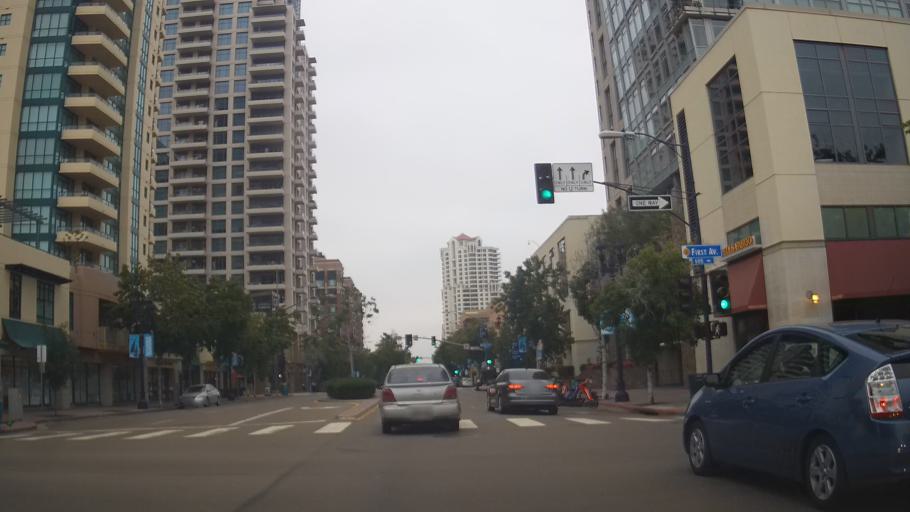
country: US
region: California
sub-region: San Diego County
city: San Diego
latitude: 32.7116
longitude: -117.1637
